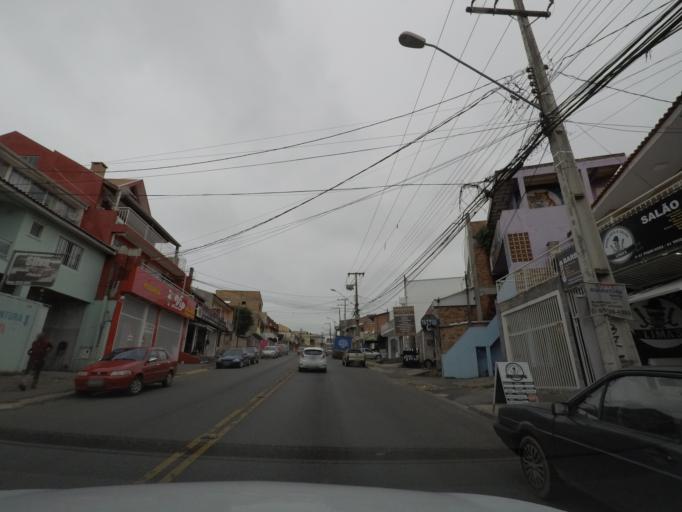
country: BR
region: Parana
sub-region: Curitiba
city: Curitiba
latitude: -25.4607
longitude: -49.3421
